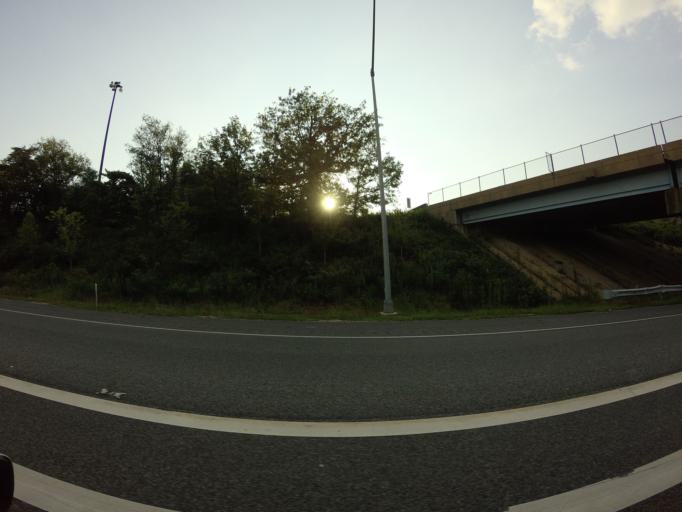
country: US
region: Maryland
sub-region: Prince George's County
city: West Laurel
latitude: 39.0992
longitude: -76.8903
